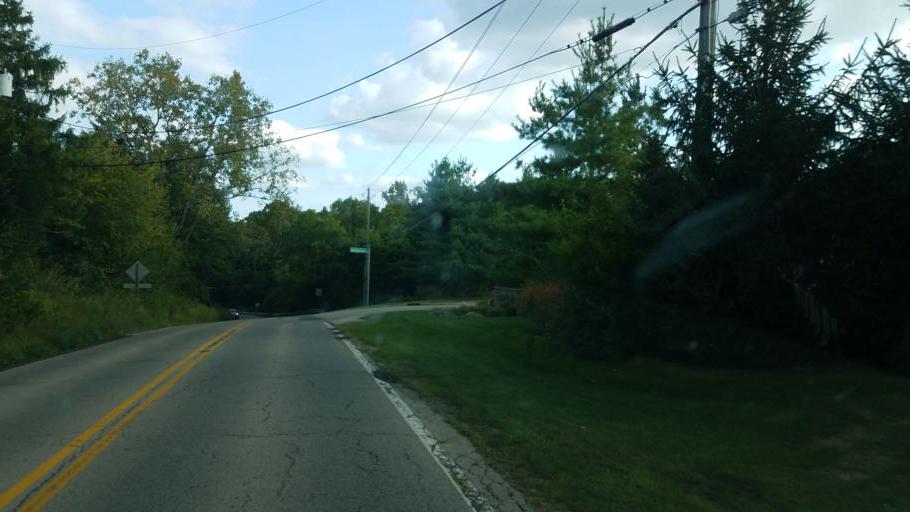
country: US
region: Ohio
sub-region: Franklin County
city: Worthington
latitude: 40.0772
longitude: -83.0472
